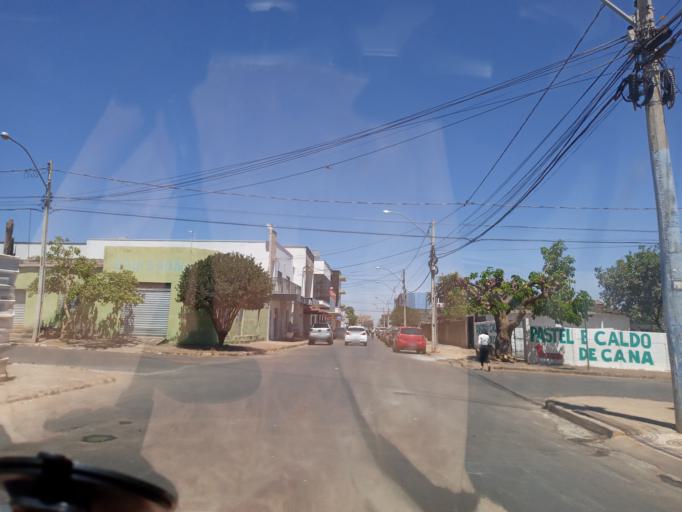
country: BR
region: Goias
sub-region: Abadiania
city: Abadiania
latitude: -16.0872
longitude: -48.5065
